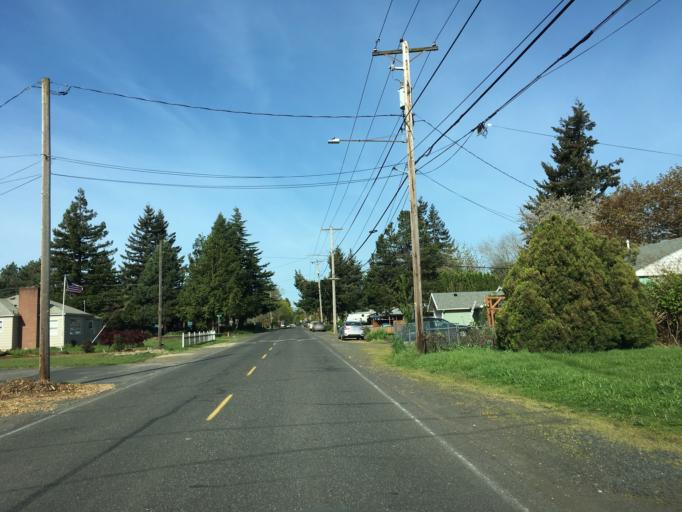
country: US
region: Oregon
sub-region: Multnomah County
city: Lents
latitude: 45.5372
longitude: -122.5395
